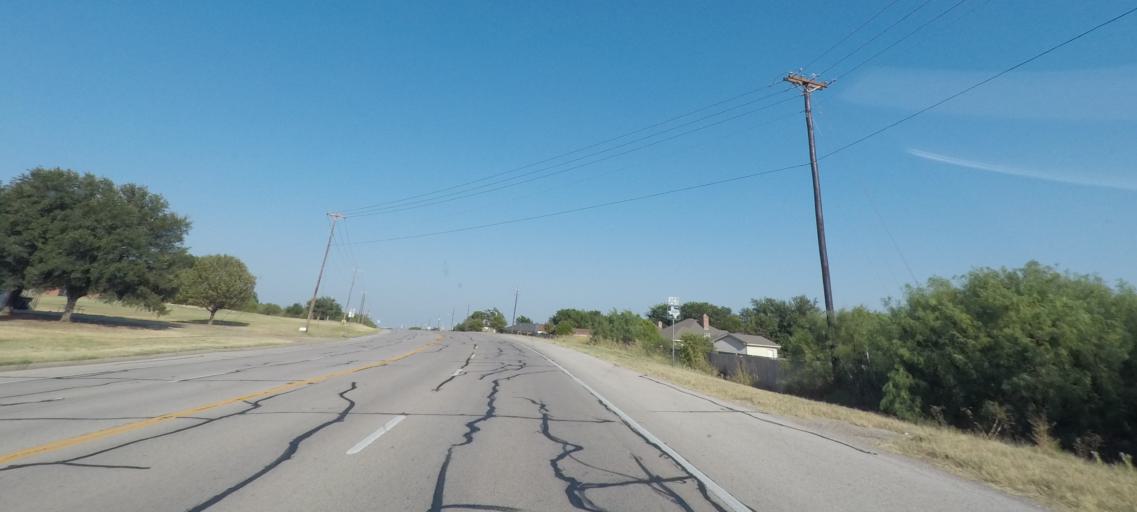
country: US
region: Texas
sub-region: Archer County
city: Holliday
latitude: 33.8595
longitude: -98.5991
